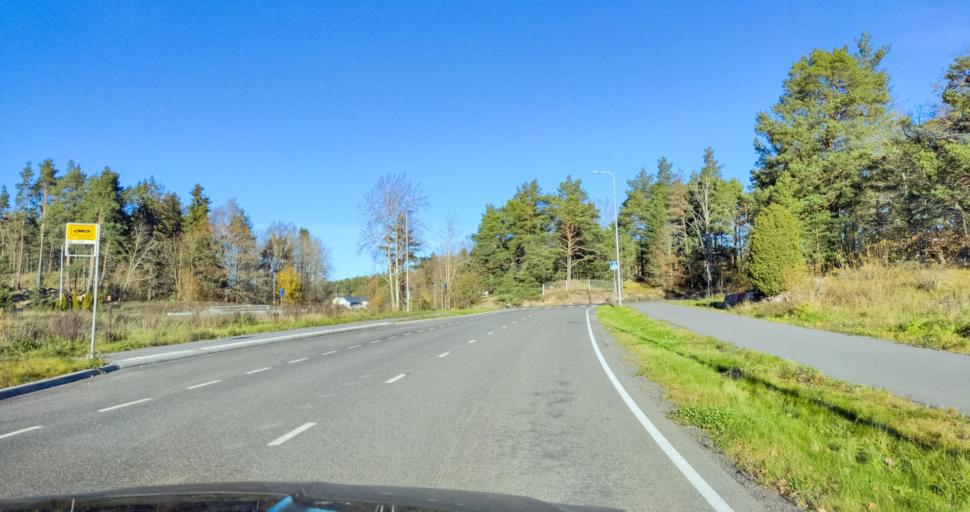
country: FI
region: Varsinais-Suomi
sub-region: Turku
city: Turku
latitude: 60.4072
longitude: 22.2080
